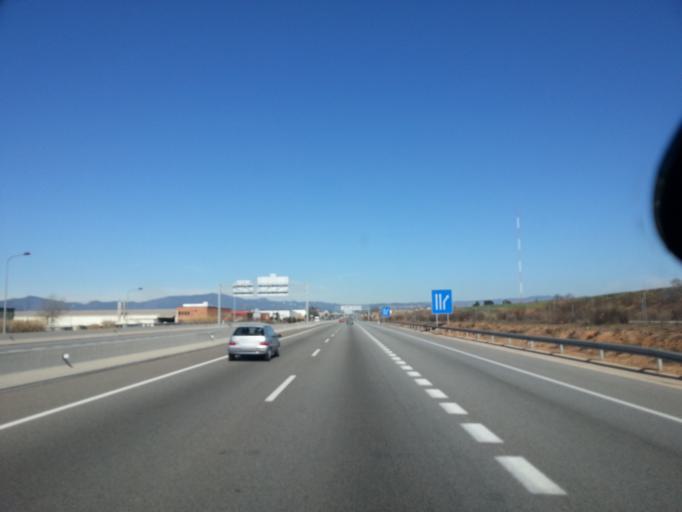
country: ES
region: Catalonia
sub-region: Provincia de Barcelona
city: Santa Perpetua de Mogoda
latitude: 41.5480
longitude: 2.1867
